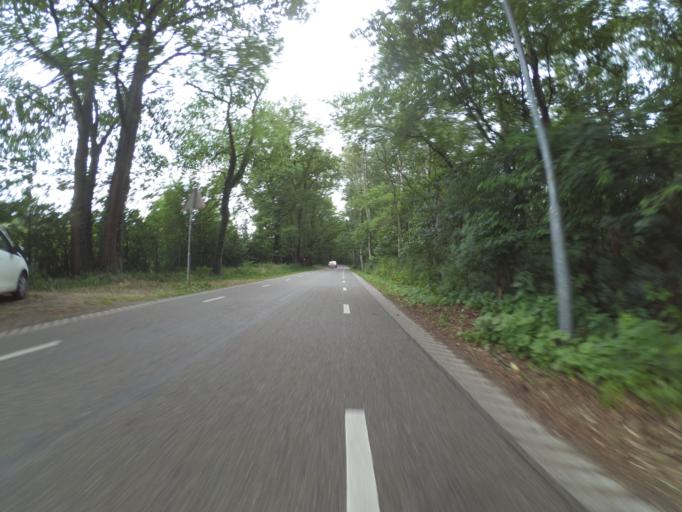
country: NL
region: Gelderland
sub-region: Gemeente Brummen
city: Eerbeek
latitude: 52.0940
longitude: 6.0453
